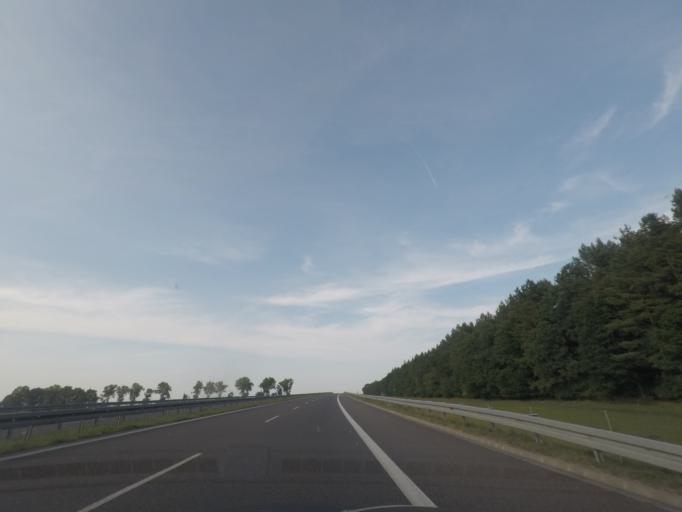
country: PL
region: West Pomeranian Voivodeship
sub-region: Powiat goleniowski
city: Nowogard
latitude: 53.6688
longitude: 15.0773
